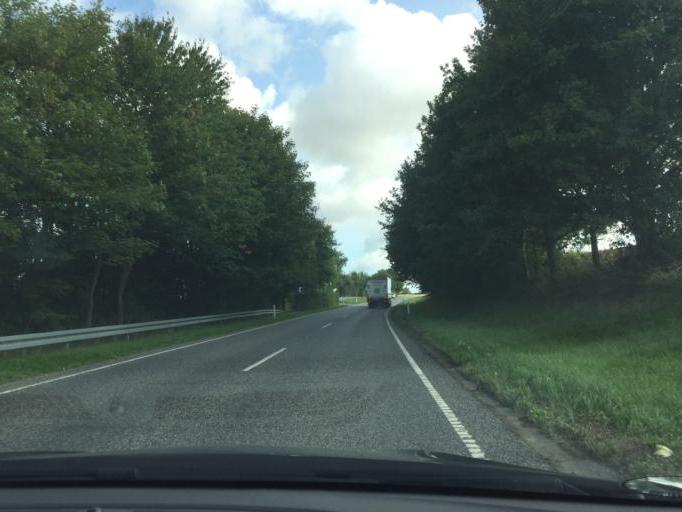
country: DK
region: Central Jutland
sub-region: Odder Kommune
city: Odder
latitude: 55.9080
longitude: 10.0318
